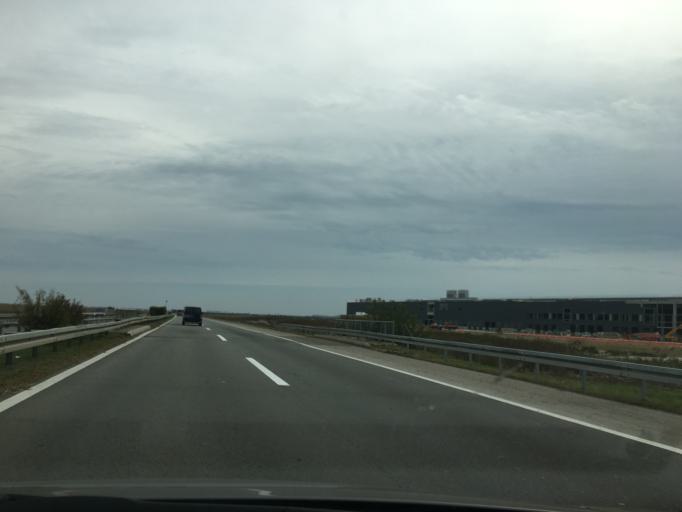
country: RS
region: Autonomna Pokrajina Vojvodina
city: Nova Pazova
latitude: 44.9667
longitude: 20.2397
